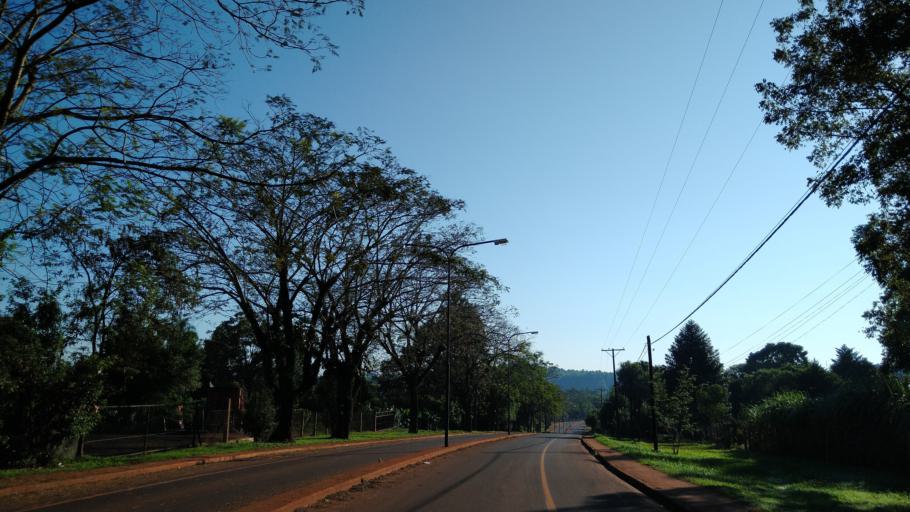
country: AR
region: Misiones
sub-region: Departamento de Montecarlo
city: Montecarlo
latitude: -26.5746
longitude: -54.7450
